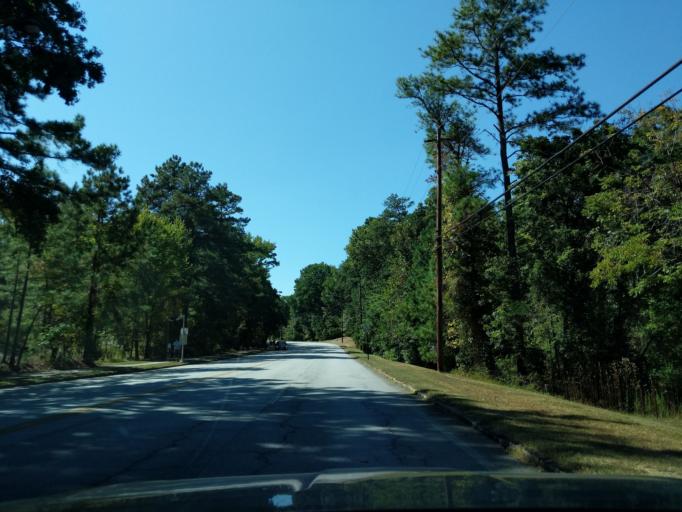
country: US
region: Georgia
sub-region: DeKalb County
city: Stone Mountain
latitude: 33.8127
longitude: -84.1547
